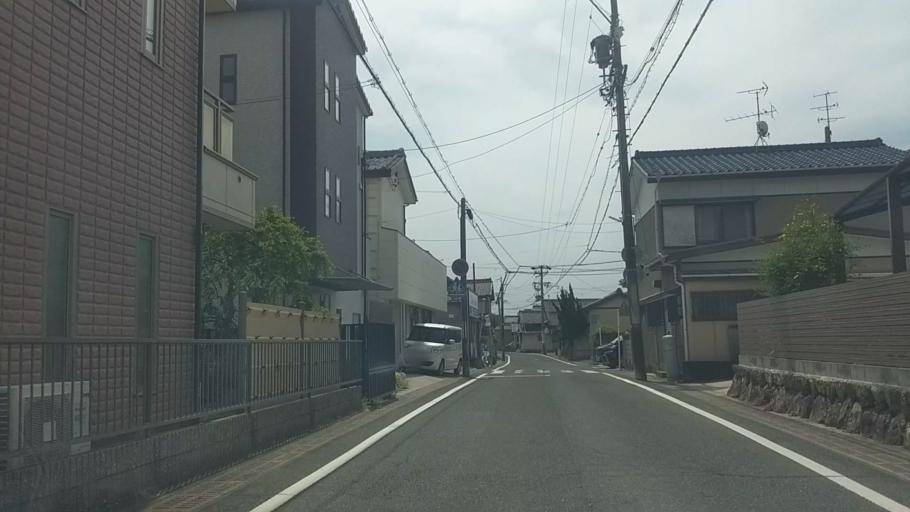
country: JP
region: Shizuoka
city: Kosai-shi
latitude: 34.7493
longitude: 137.5288
